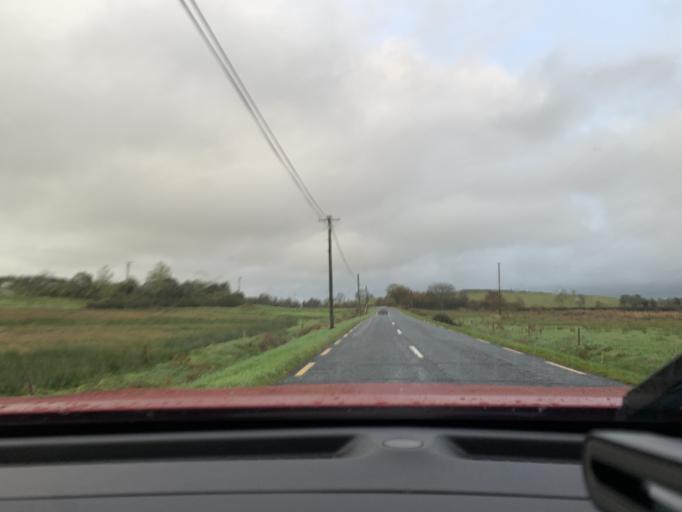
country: IE
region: Connaught
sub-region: Sligo
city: Ballymote
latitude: 54.0225
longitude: -8.5231
